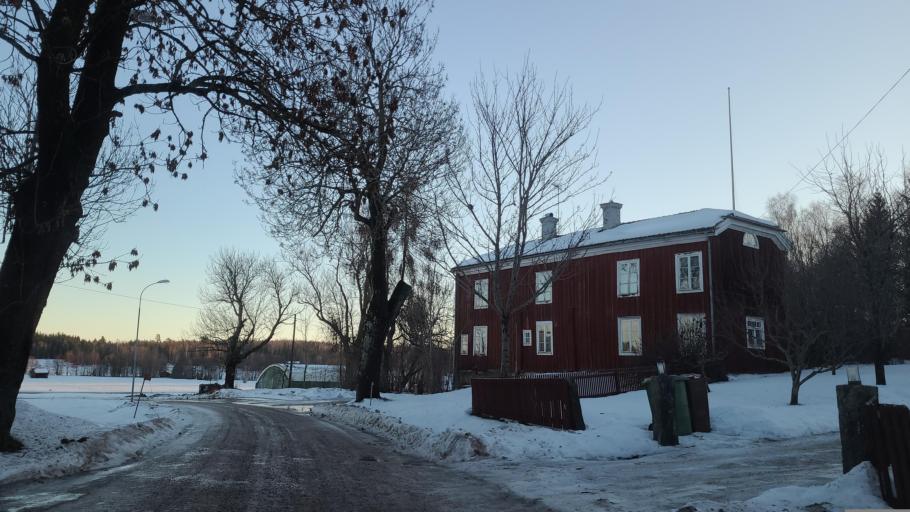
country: SE
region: Gaevleborg
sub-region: Soderhamns Kommun
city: Soderhamn
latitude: 61.2724
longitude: 16.9941
